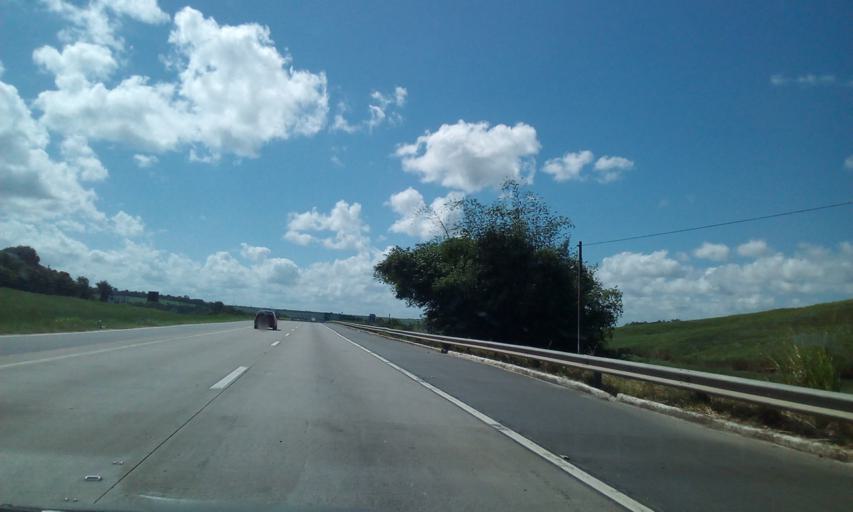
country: BR
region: Pernambuco
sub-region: Itapissuma
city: Itapissuma
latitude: -7.7716
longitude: -34.9348
